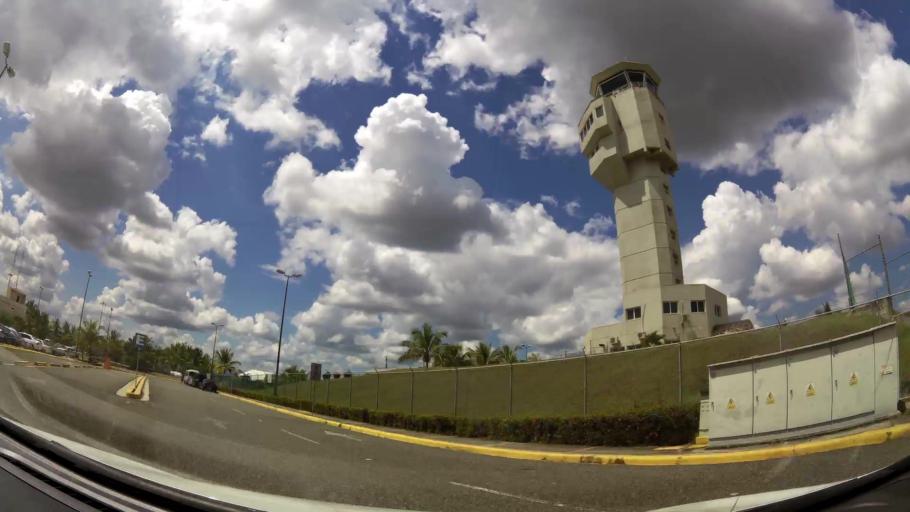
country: DO
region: Nacional
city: Santo Domingo
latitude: 18.5762
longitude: -69.9806
